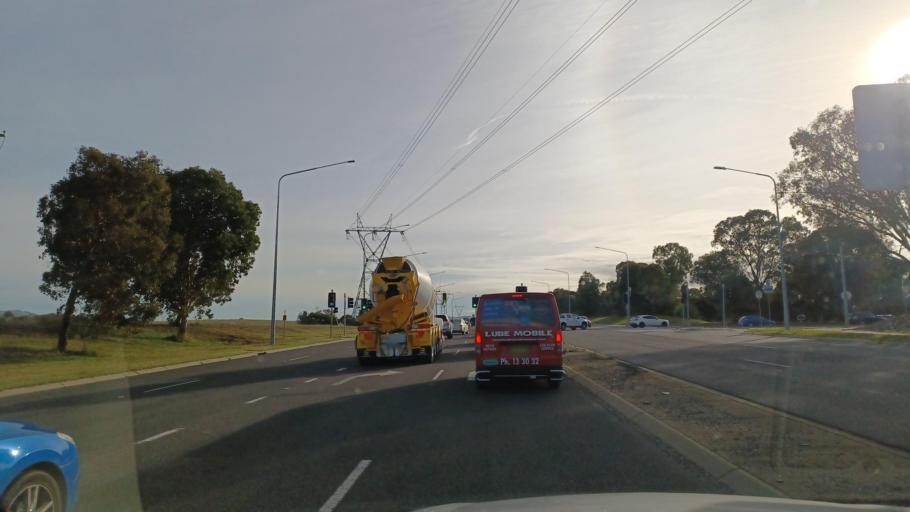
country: AU
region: Australian Capital Territory
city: Kaleen
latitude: -35.2189
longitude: 149.1307
